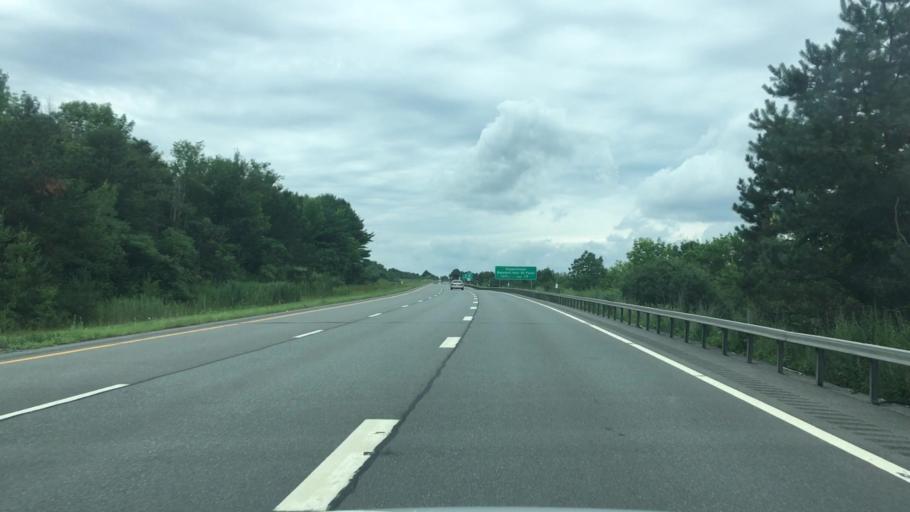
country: US
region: New York
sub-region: Albany County
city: Altamont
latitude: 42.7719
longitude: -74.0844
